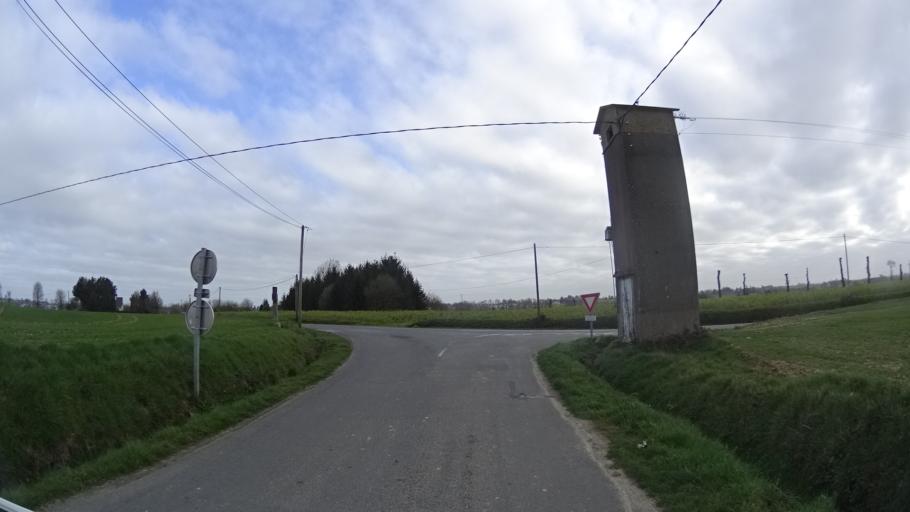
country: FR
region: Brittany
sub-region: Departement d'Ille-et-Vilaine
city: Saint-Gilles
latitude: 48.1842
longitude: -1.8342
